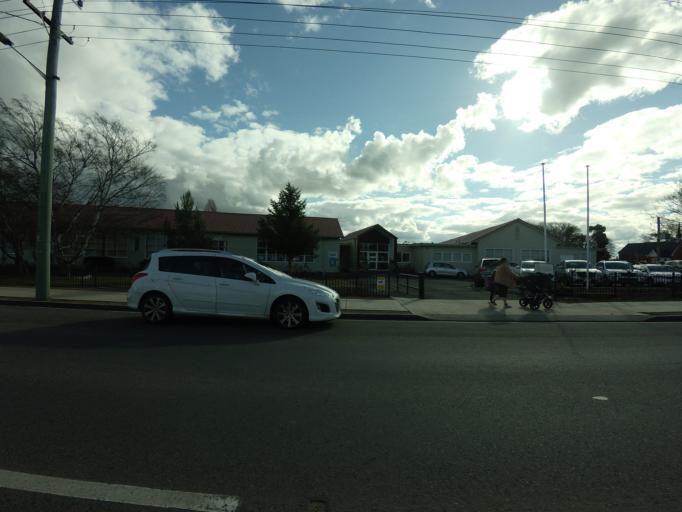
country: AU
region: Tasmania
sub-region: Northern Midlands
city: Longford
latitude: -41.6904
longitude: 147.0794
